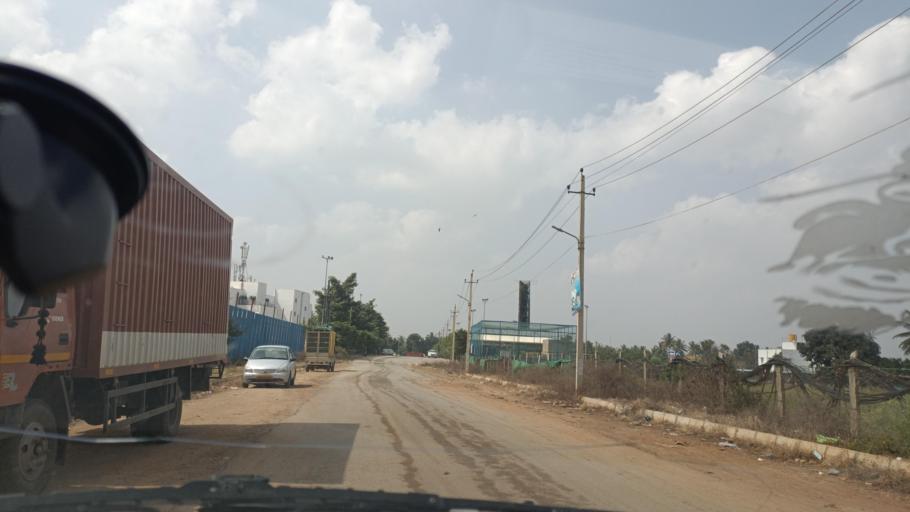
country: IN
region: Karnataka
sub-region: Bangalore Urban
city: Yelahanka
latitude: 13.1690
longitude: 77.6341
